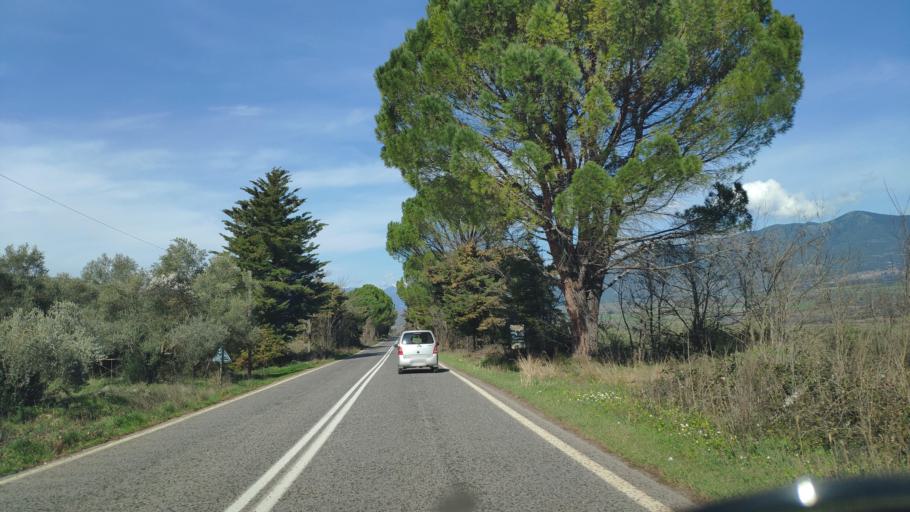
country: GR
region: Central Greece
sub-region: Nomos Fthiotidos
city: Amfikleia
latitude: 38.6514
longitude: 22.5823
